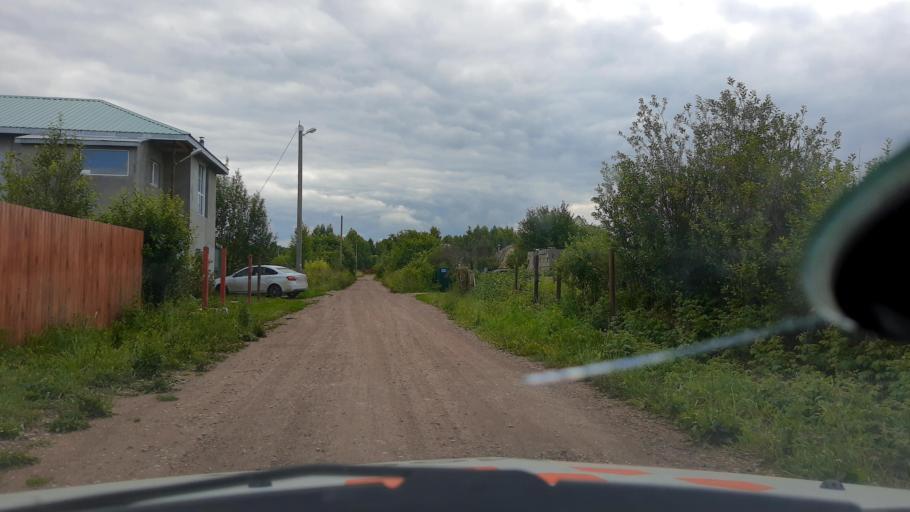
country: RU
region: Bashkortostan
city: Kabakovo
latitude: 54.7211
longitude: 56.2081
